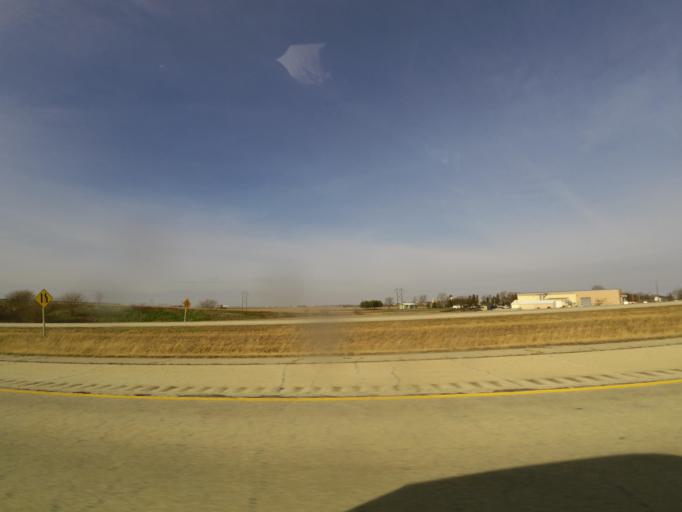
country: US
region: Illinois
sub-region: Macon County
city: Warrensburg
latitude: 39.8920
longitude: -89.0100
